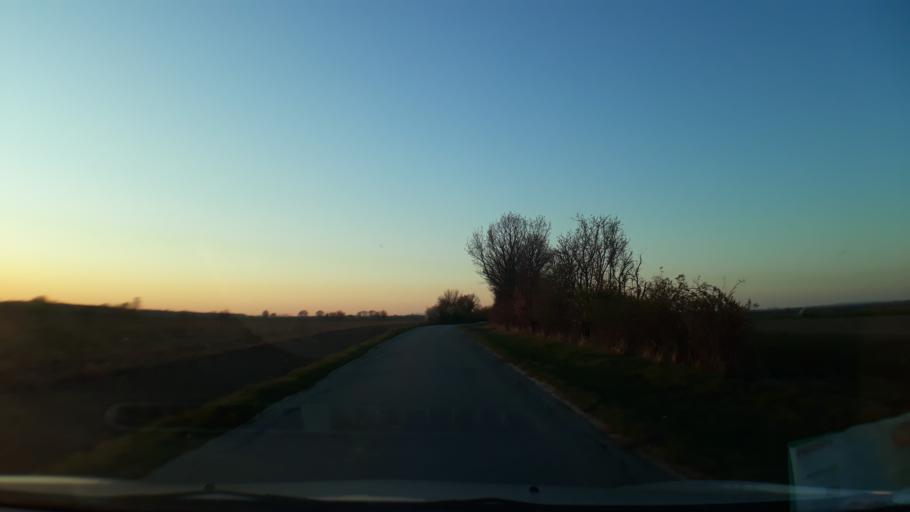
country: DE
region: North Rhine-Westphalia
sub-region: Regierungsbezirk Koln
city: Vettweiss
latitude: 50.7166
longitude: 6.6120
